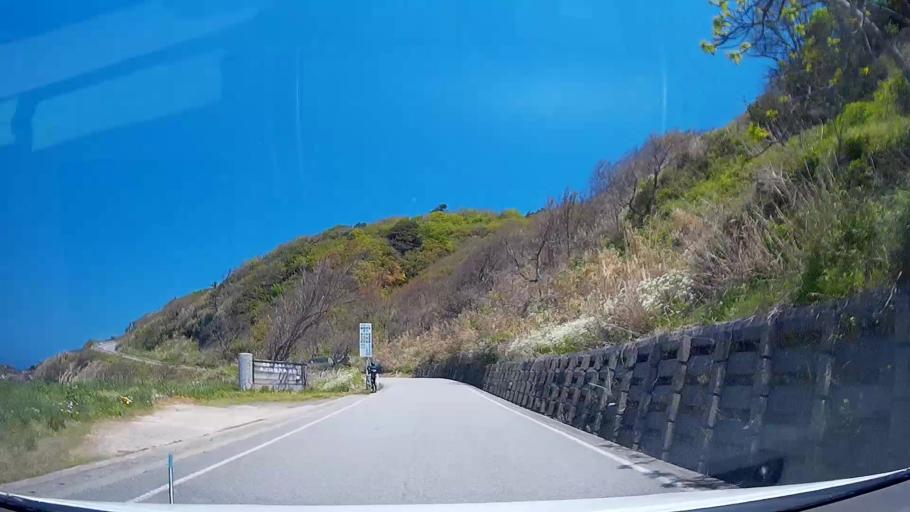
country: JP
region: Ishikawa
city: Nanao
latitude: 37.5216
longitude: 137.2472
